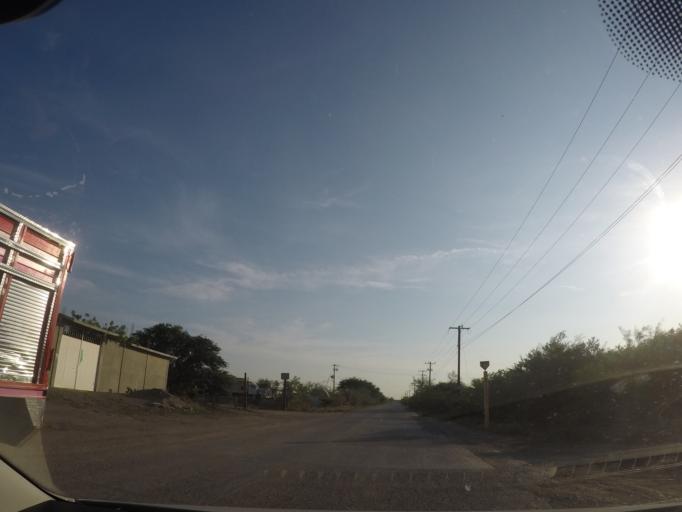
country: MX
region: Oaxaca
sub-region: Salina Cruz
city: Salina Cruz
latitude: 16.2232
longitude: -95.1883
